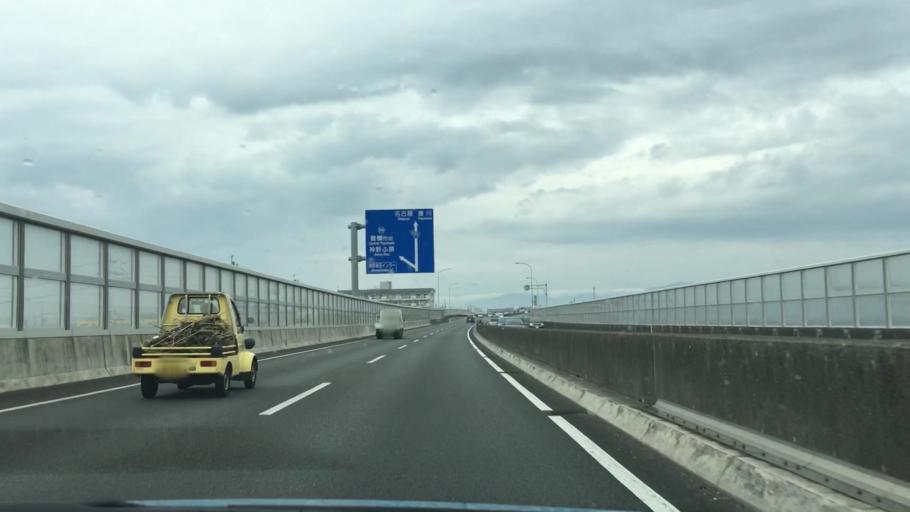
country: JP
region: Aichi
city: Toyohashi
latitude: 34.7354
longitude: 137.3474
